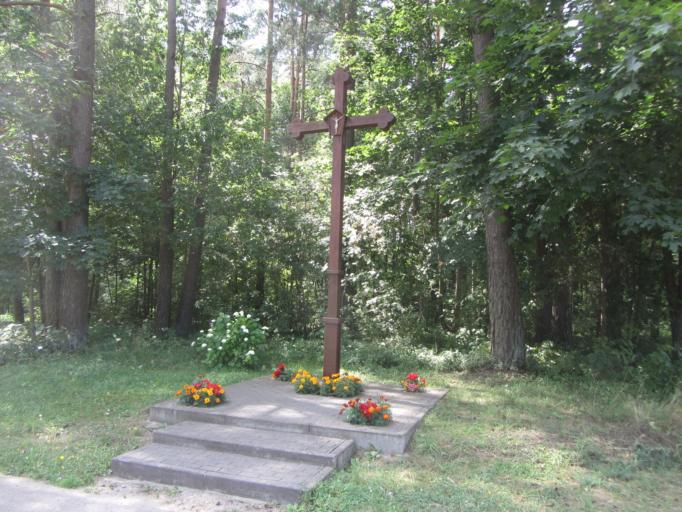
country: LT
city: Baltoji Voke
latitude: 54.5848
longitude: 25.2663
